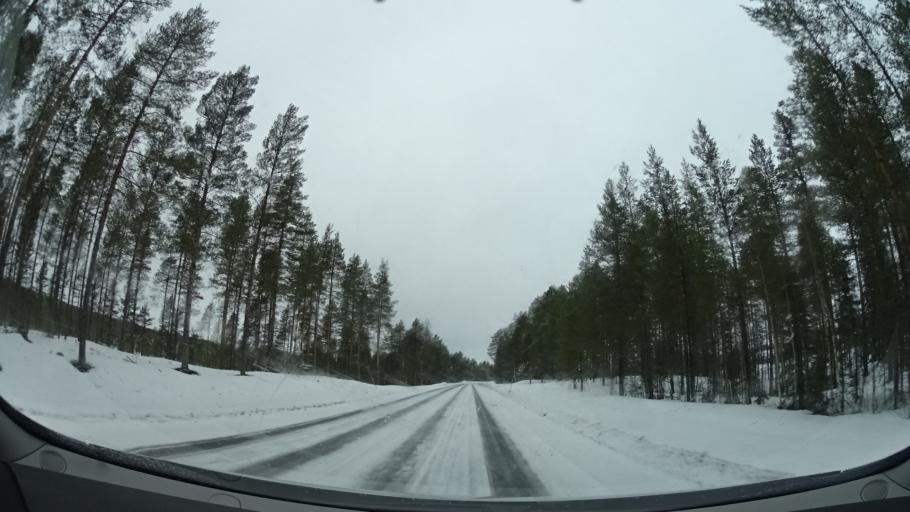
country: SE
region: Vaesterbotten
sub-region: Mala Kommun
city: Mala
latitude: 65.1495
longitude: 18.8128
